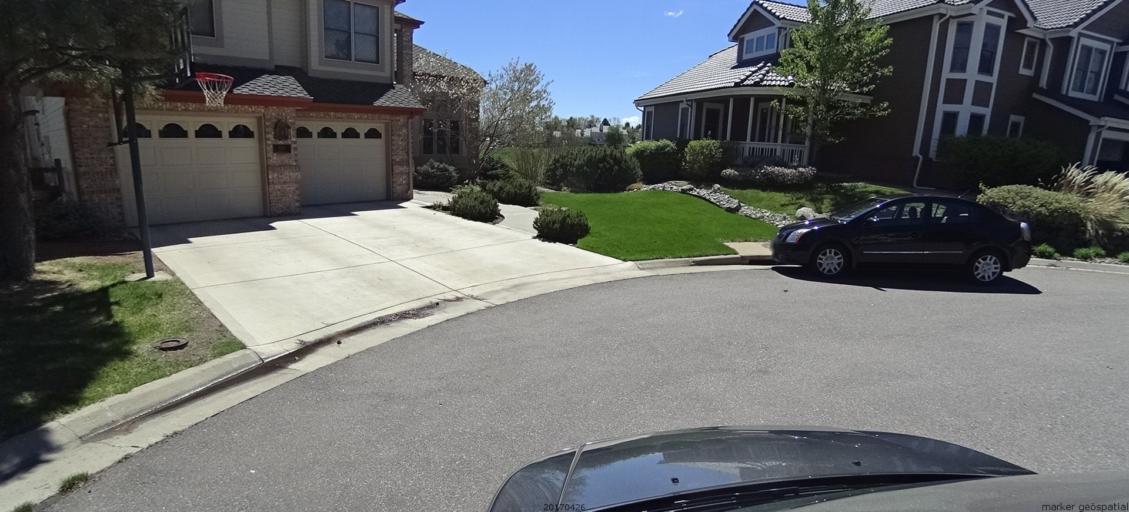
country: US
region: Colorado
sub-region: Adams County
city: Lone Tree
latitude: 39.5477
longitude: -104.8914
